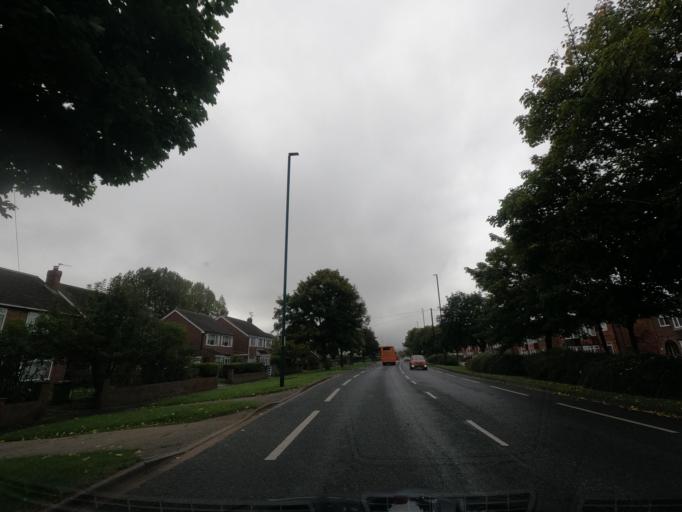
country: GB
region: England
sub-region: Redcar and Cleveland
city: Redcar
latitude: 54.6073
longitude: -1.0836
